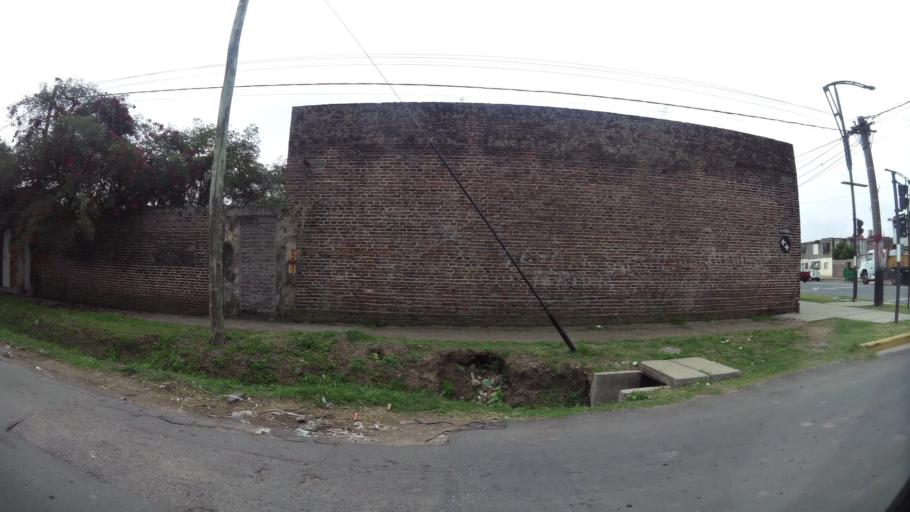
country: AR
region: Santa Fe
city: Gobernador Galvez
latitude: -33.0149
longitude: -60.6522
